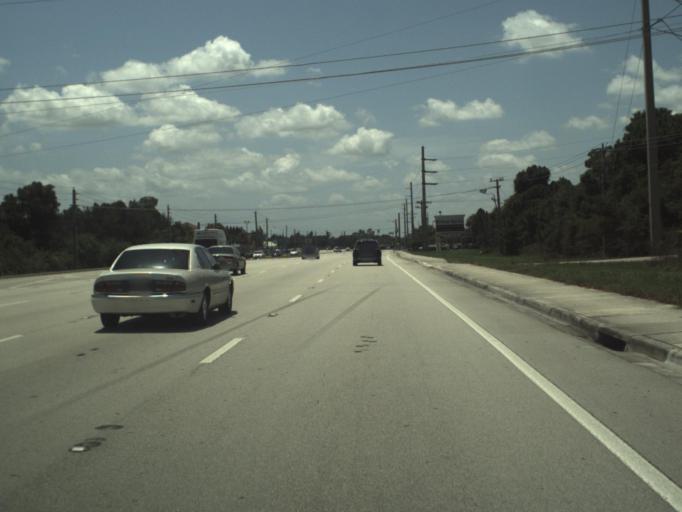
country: US
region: Florida
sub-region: Martin County
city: North River Shores
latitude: 27.2507
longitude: -80.2758
